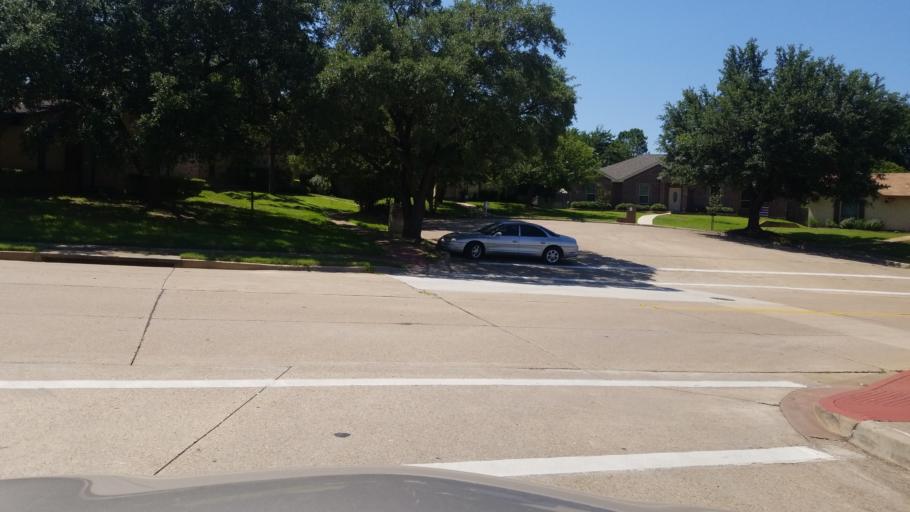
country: US
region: Texas
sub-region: Dallas County
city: Grand Prairie
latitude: 32.6925
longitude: -96.9938
